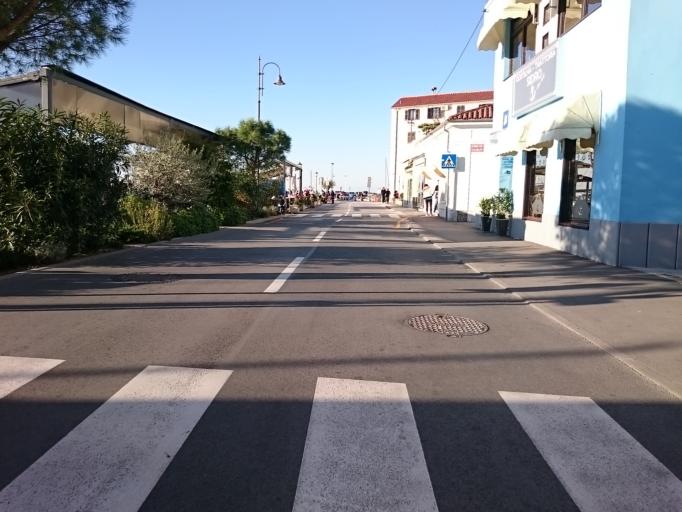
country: SI
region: Izola-Isola
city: Izola
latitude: 45.5377
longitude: 13.6573
